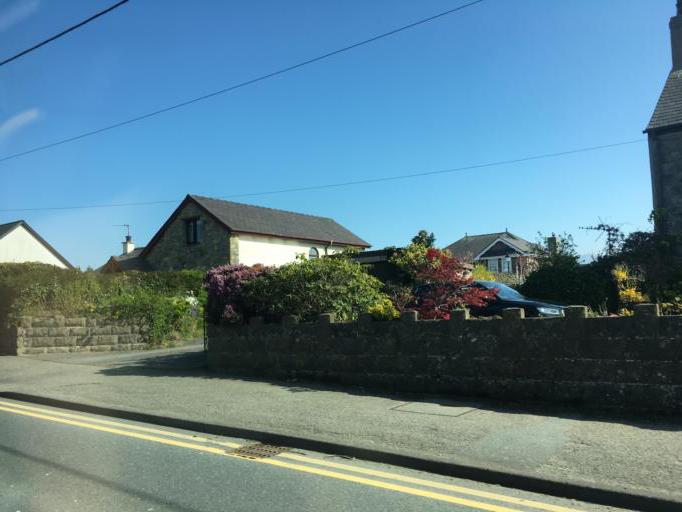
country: GB
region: Wales
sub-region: Anglesey
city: Menai Bridge
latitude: 53.2101
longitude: -4.1641
